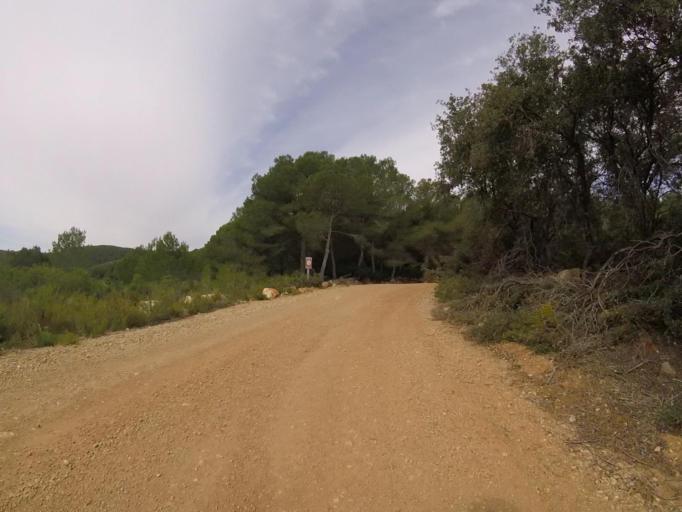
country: ES
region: Valencia
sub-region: Provincia de Castello
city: Cabanes
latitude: 40.1901
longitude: 0.0893
